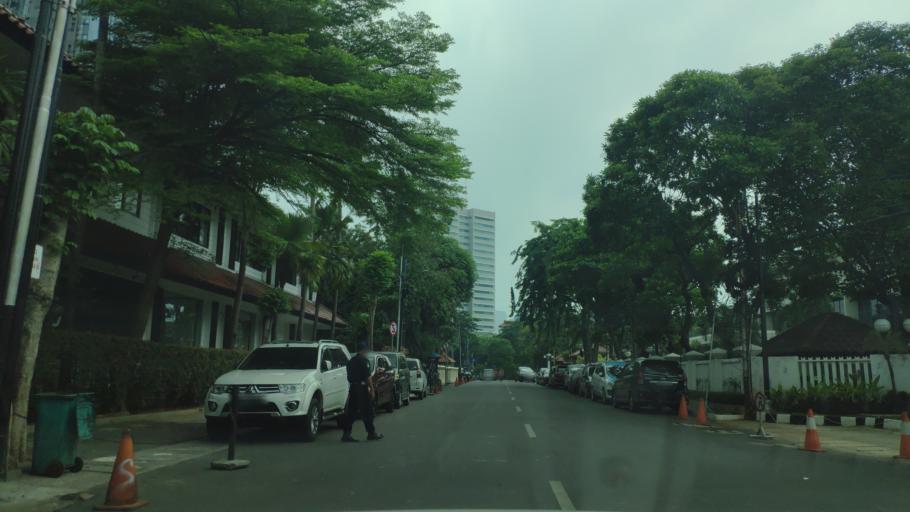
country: ID
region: Jakarta Raya
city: Jakarta
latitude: -6.2105
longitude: 106.7947
